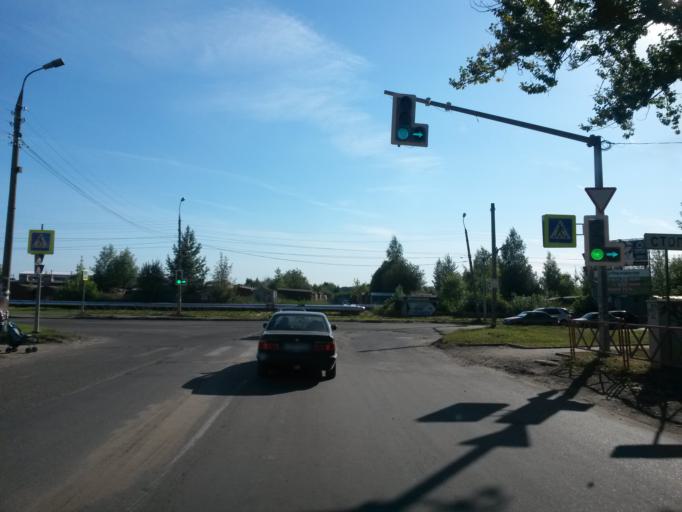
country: RU
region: Jaroslavl
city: Yaroslavl
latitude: 57.5711
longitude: 39.8590
